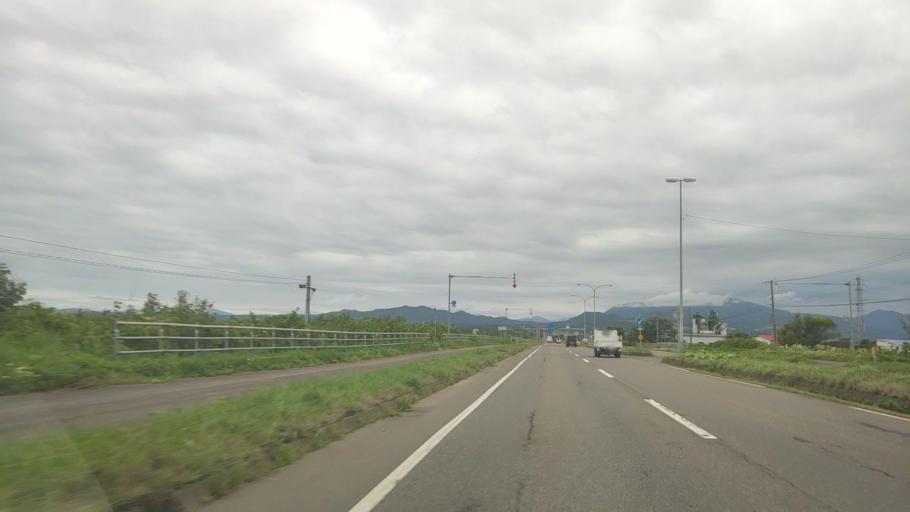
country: JP
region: Hokkaido
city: Nanae
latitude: 42.2723
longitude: 140.2725
